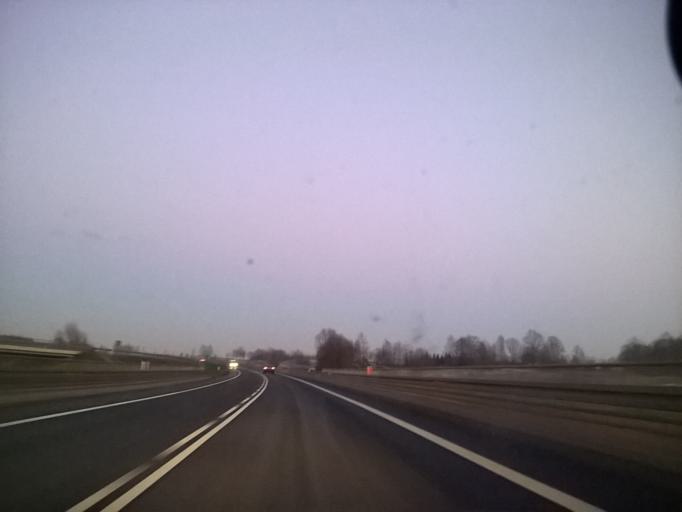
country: PL
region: Warmian-Masurian Voivodeship
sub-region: Powiat olsztynski
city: Biskupiec
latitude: 53.8330
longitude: 20.9155
